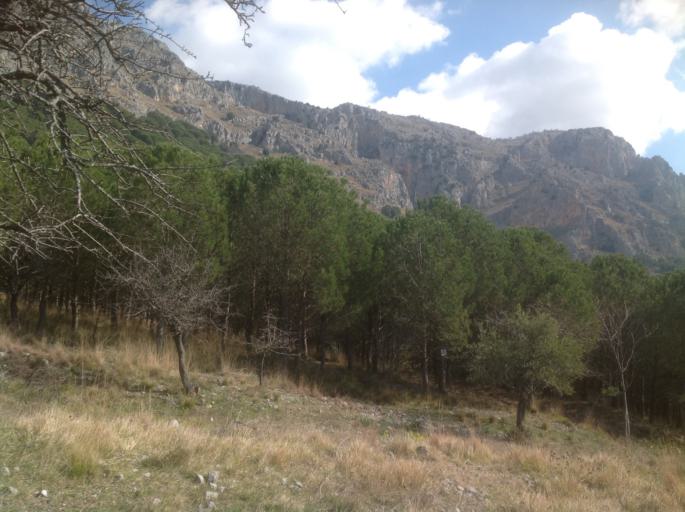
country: IT
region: Calabria
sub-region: Provincia di Cosenza
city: Frascineto
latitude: 39.8366
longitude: 16.2671
